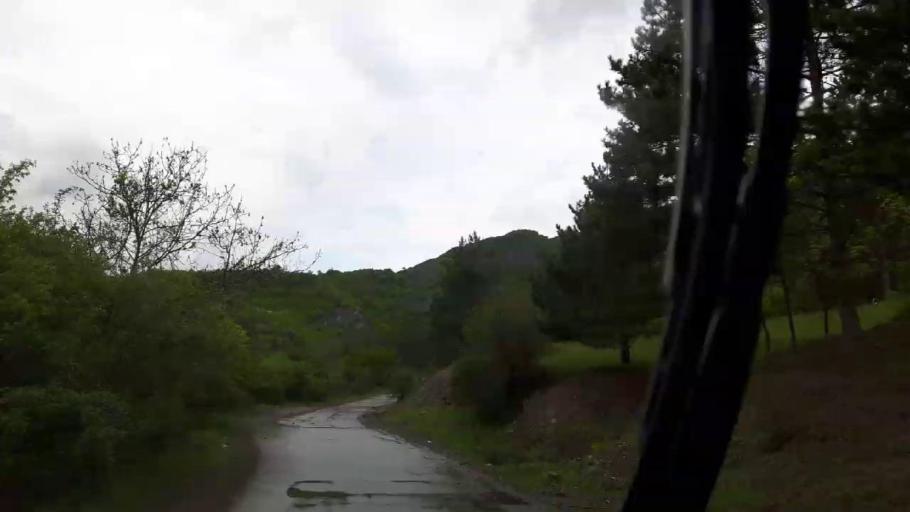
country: GE
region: Shida Kartli
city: Gori
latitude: 41.8991
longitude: 44.0477
